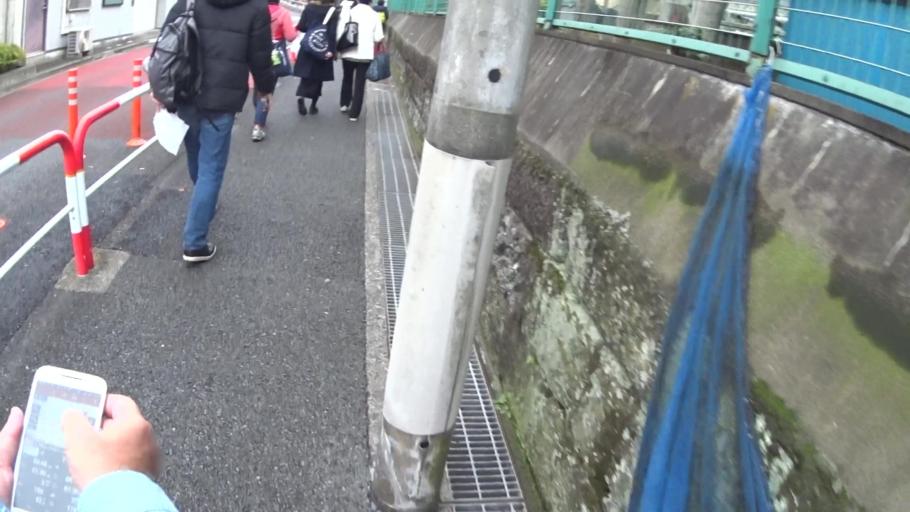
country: JP
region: Tokyo
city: Tokyo
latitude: 35.6953
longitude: 139.7103
